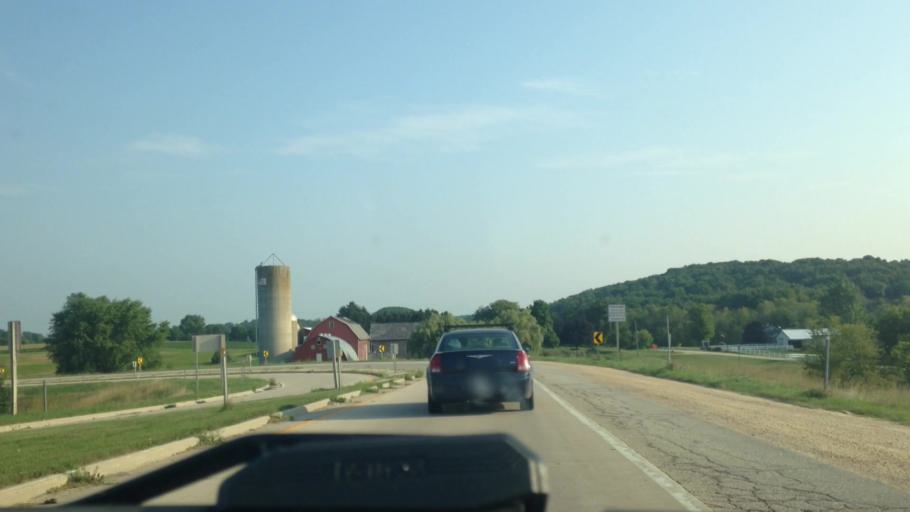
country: US
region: Wisconsin
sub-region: Dodge County
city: Theresa
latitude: 43.5375
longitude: -88.4011
